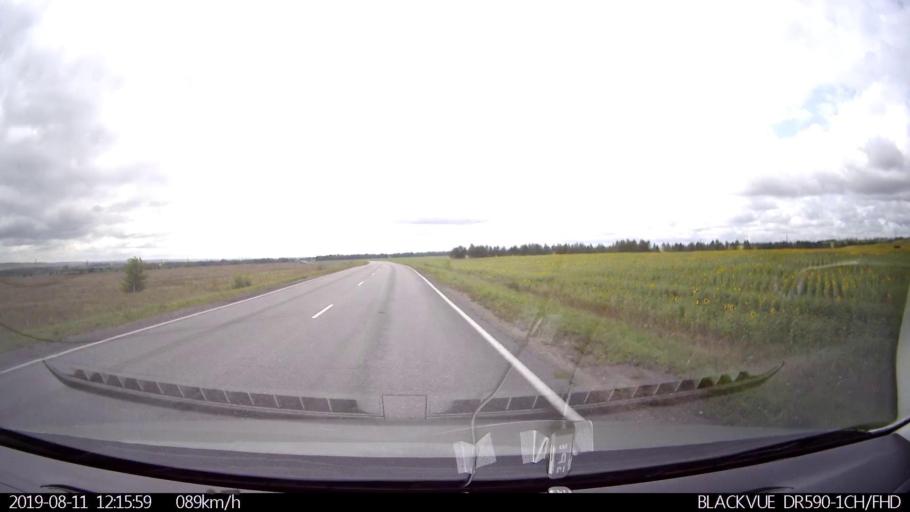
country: RU
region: Ulyanovsk
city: Ignatovka
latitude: 53.9355
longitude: 47.9630
